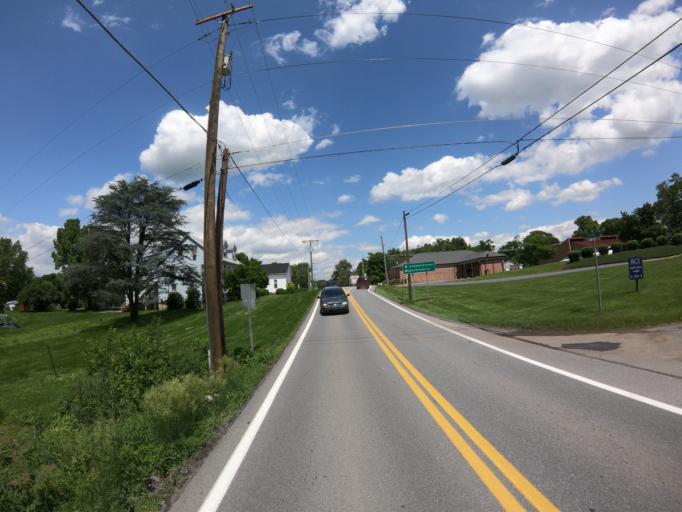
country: US
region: West Virginia
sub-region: Jefferson County
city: Shepherdstown
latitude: 39.3871
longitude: -77.8869
